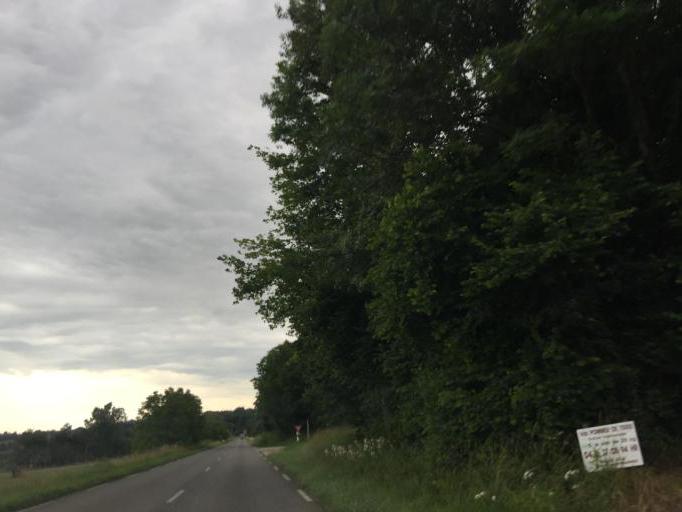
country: FR
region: Rhone-Alpes
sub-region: Departement de la Savoie
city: Domessin
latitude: 45.5161
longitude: 5.7064
